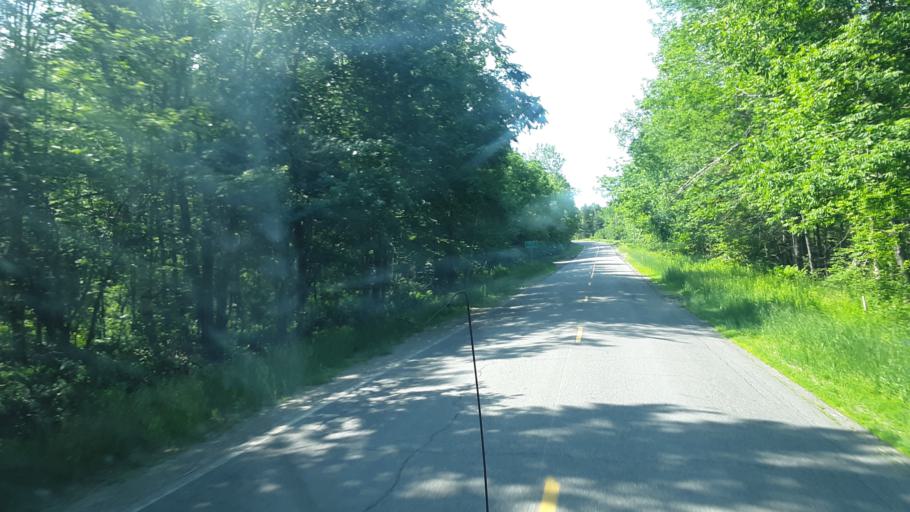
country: US
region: Maine
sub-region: Waldo County
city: Swanville
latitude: 44.5639
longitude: -68.9536
